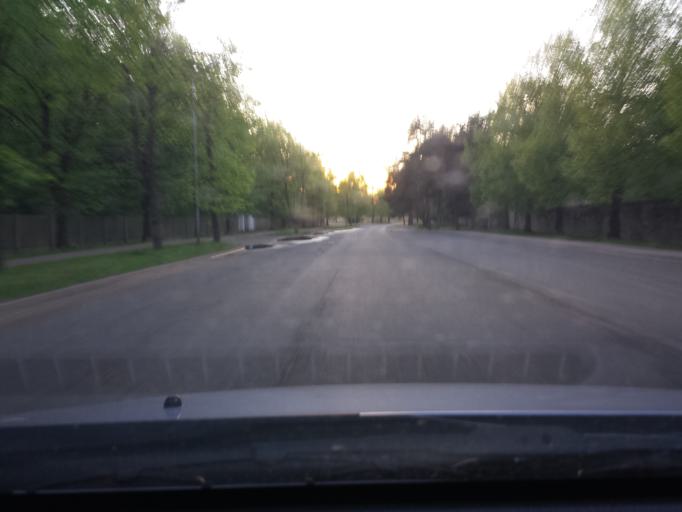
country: LV
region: Riga
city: Riga
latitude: 56.9862
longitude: 24.1446
